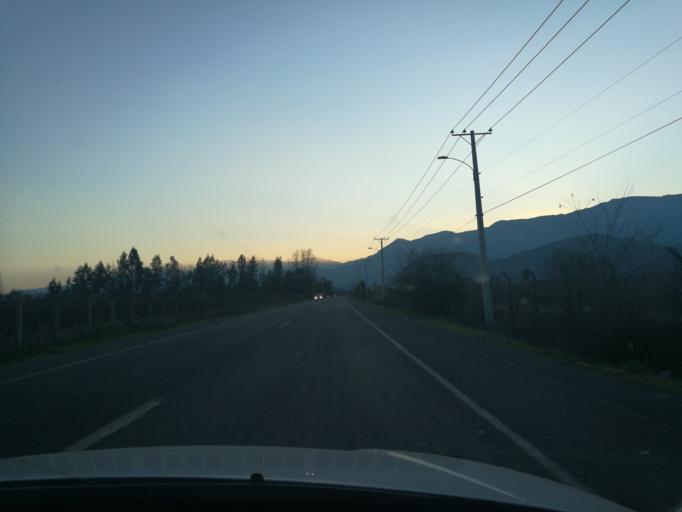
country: CL
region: O'Higgins
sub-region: Provincia de Cachapoal
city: Graneros
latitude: -34.0385
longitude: -70.6911
